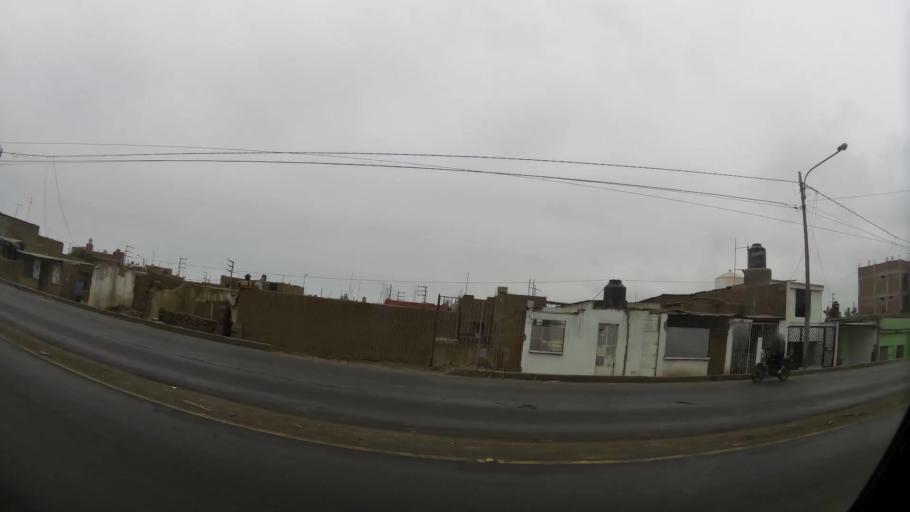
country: PE
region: La Libertad
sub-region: Provincia de Trujillo
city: Moche
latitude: -8.1515
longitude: -79.0115
